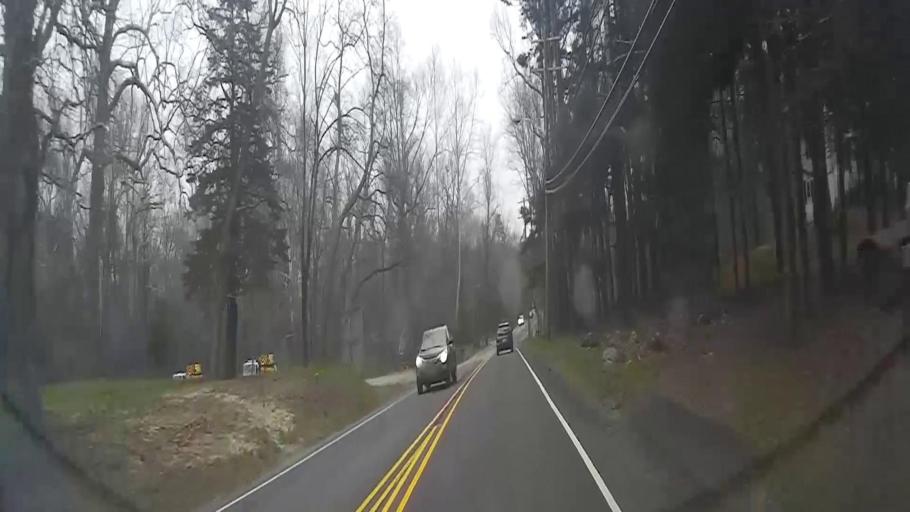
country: US
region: New Jersey
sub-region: Burlington County
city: Medford Lakes
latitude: 39.8790
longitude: -74.8609
